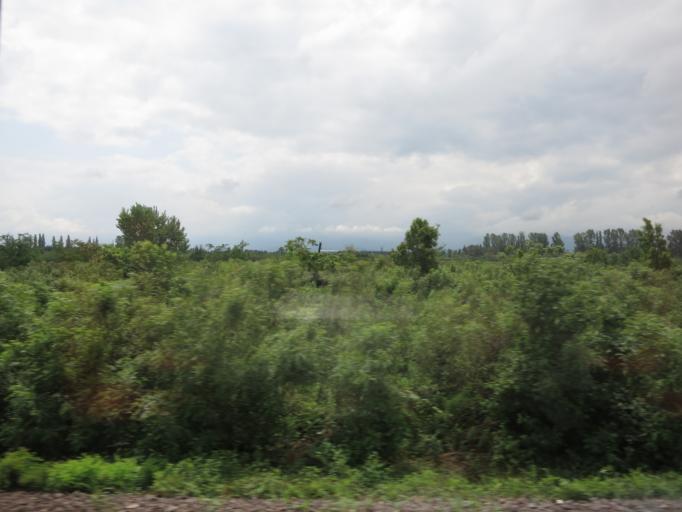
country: GE
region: Imereti
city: K'ulashi
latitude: 42.1822
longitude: 42.4380
